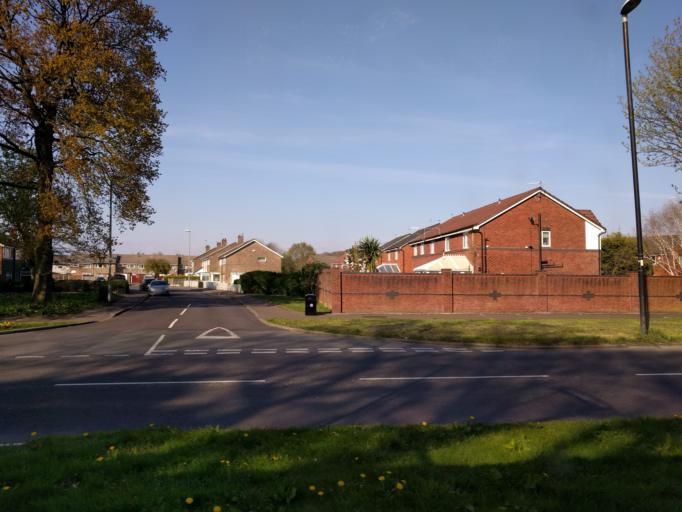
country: GB
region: England
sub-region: Manchester
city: Ringway
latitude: 53.3757
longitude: -2.2544
